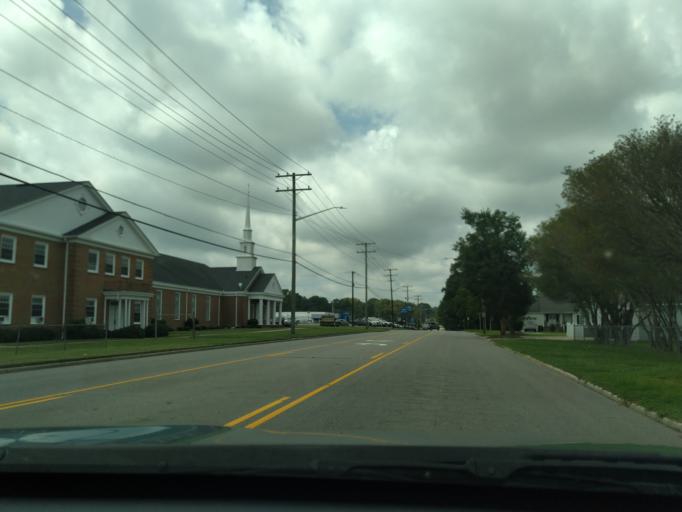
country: US
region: North Carolina
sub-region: Edgecombe County
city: Tarboro
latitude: 35.8957
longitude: -77.5454
